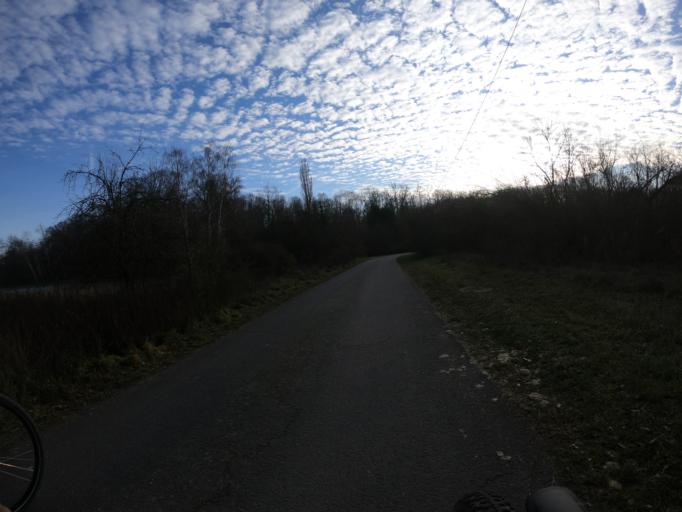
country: DE
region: Hesse
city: Morfelden-Walldorf
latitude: 49.9651
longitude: 8.5640
